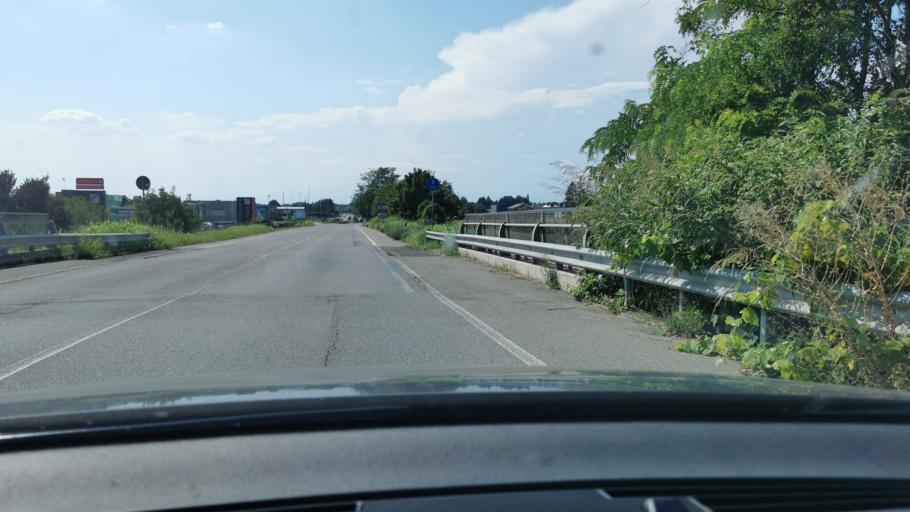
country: IT
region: Lombardy
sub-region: Provincia di Como
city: Cirimido
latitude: 45.6944
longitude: 9.0152
